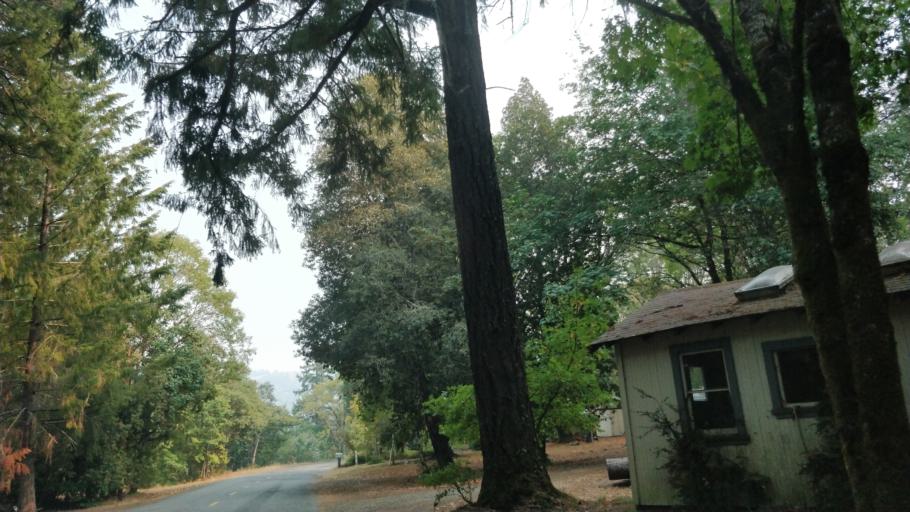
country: US
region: California
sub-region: Humboldt County
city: Rio Dell
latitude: 40.2355
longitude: -124.1574
